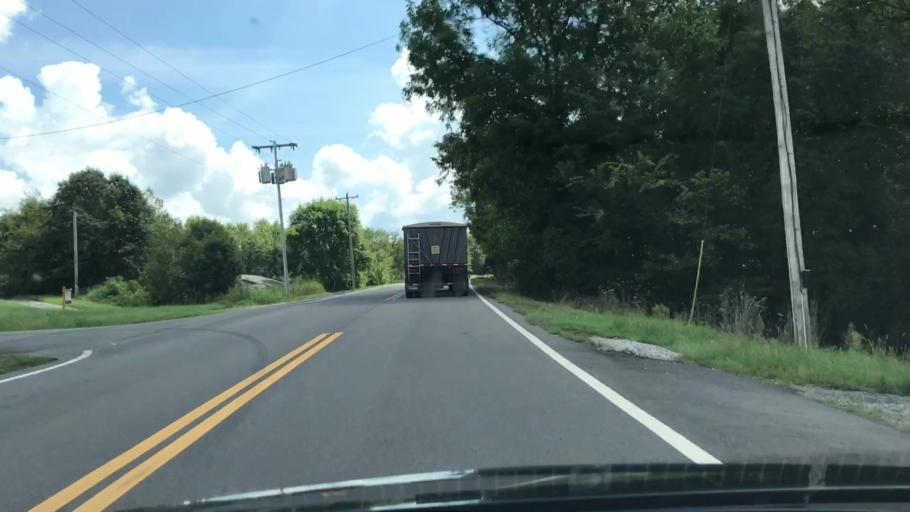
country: US
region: Tennessee
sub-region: Robertson County
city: Springfield
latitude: 36.6297
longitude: -86.9572
